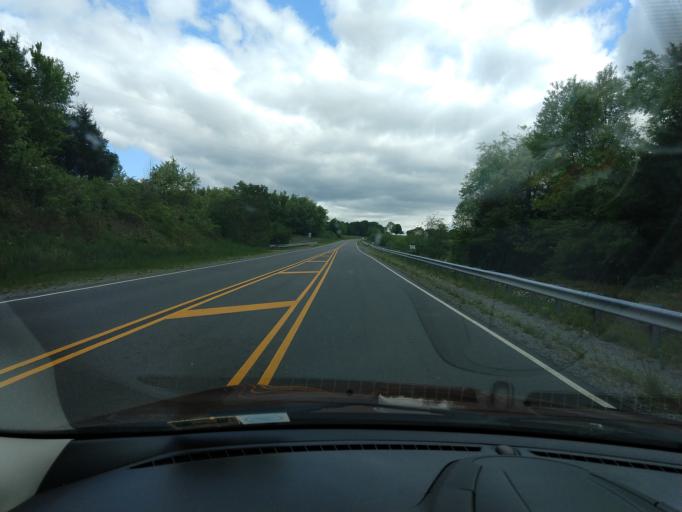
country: US
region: Virginia
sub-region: Wythe County
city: Wytheville
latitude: 36.8742
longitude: -80.9831
